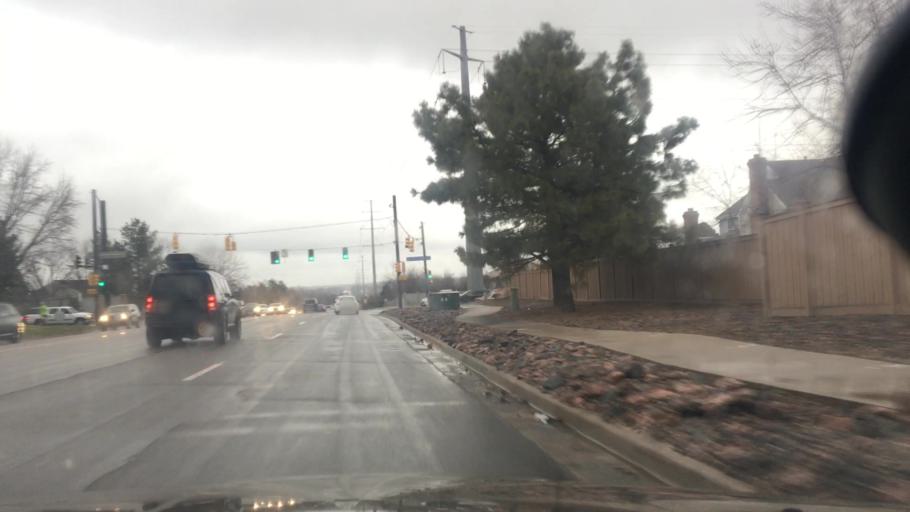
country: US
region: Colorado
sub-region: Arapahoe County
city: Castlewood
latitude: 39.5799
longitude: -104.9226
